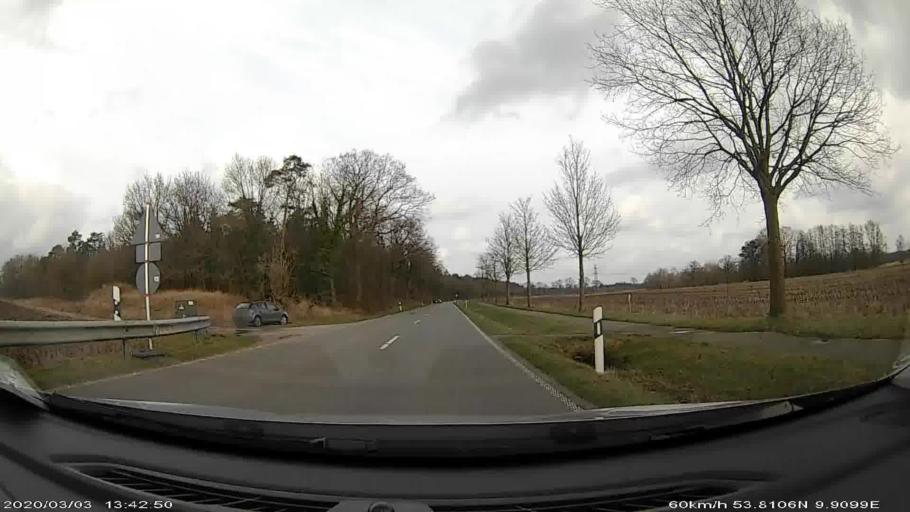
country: DE
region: Schleswig-Holstein
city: Alveslohe
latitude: 53.8113
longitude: 9.9115
